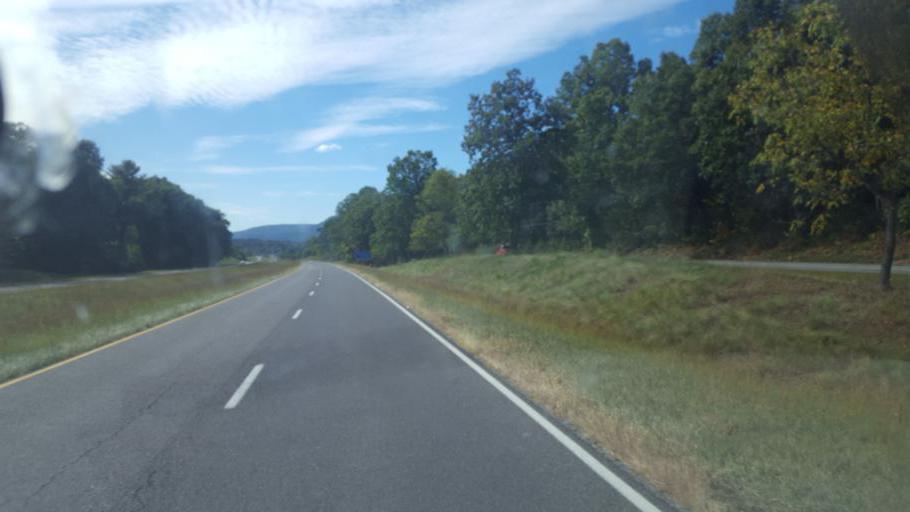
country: US
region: Virginia
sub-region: Page County
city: Luray
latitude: 38.6765
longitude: -78.4329
